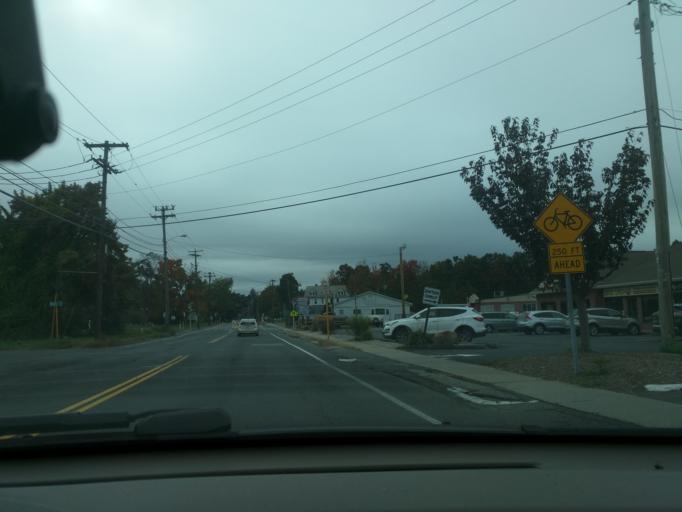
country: US
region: Massachusetts
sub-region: Hampden County
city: East Longmeadow
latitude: 42.0637
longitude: -72.5158
